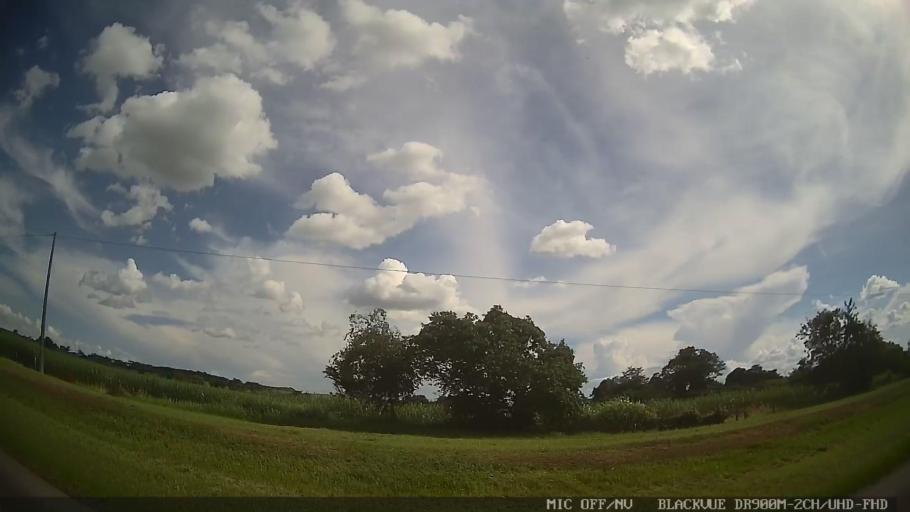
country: BR
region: Sao Paulo
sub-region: Conchas
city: Conchas
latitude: -23.0454
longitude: -47.9337
